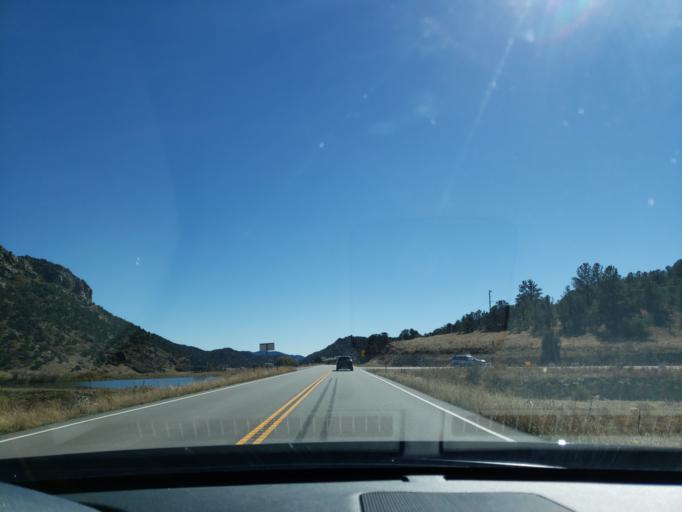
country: US
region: Colorado
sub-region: Fremont County
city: Canon City
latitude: 38.6123
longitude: -105.4421
